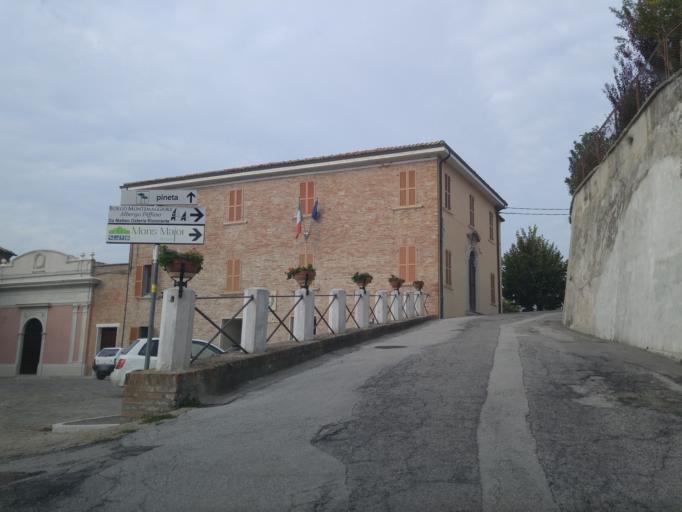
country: IT
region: The Marches
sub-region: Provincia di Pesaro e Urbino
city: Montemaggiore al Metauro
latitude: 43.7373
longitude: 12.9463
